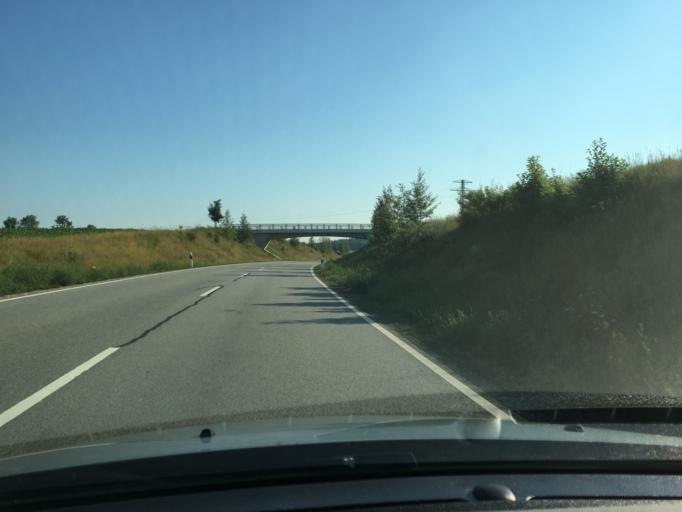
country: DE
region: Bavaria
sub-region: Upper Bavaria
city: Neumarkt-Sankt Veit
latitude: 48.3622
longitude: 12.4911
